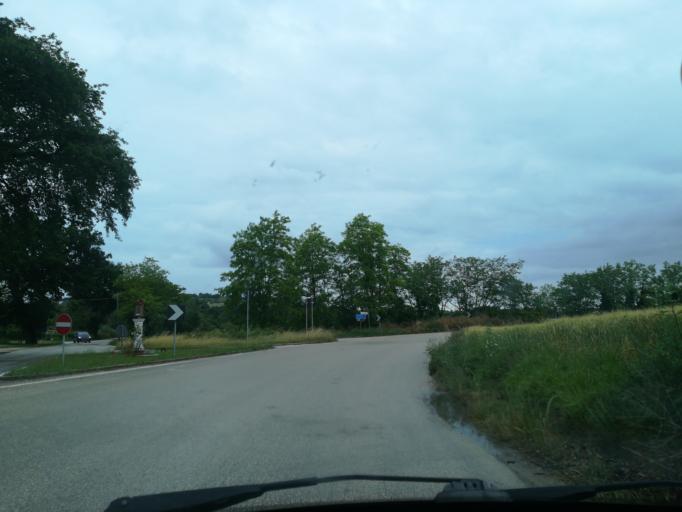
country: IT
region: The Marches
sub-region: Provincia di Macerata
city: Petriolo
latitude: 43.2331
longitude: 13.4599
